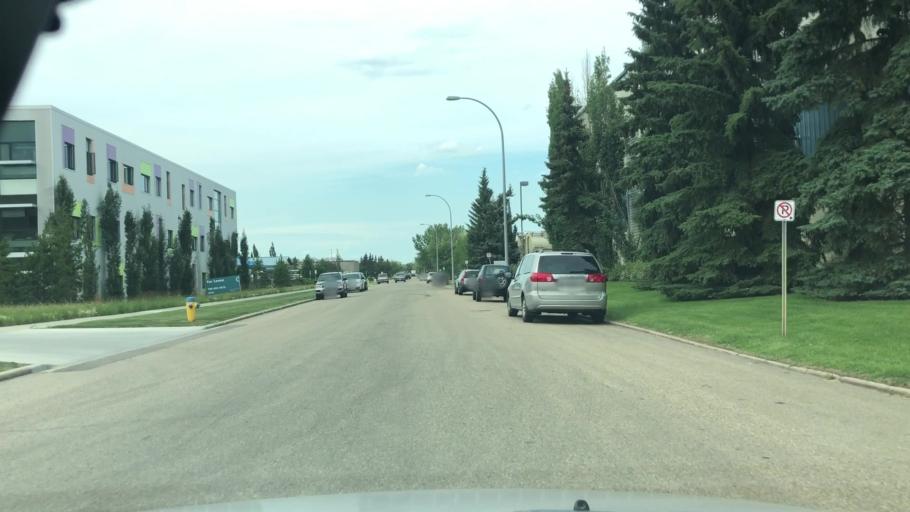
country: CA
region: Alberta
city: Edmonton
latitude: 53.5281
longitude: -113.4149
